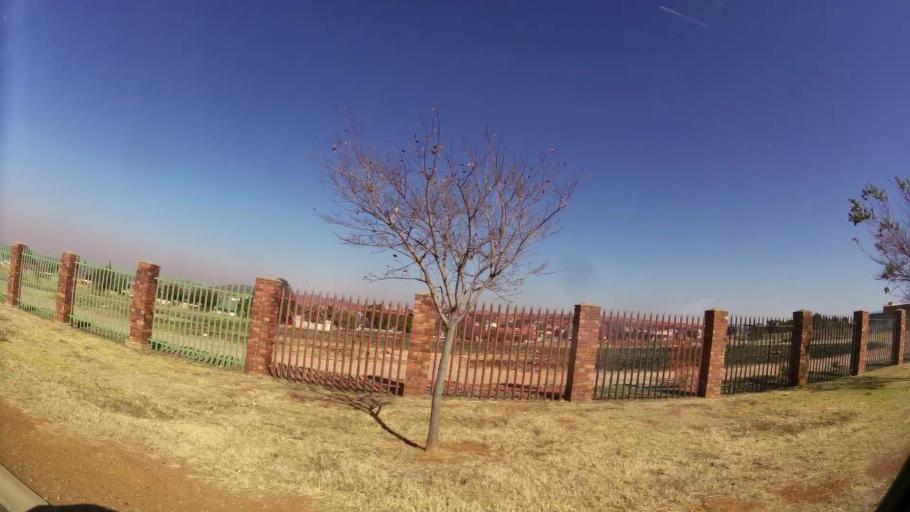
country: ZA
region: Gauteng
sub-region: Ekurhuleni Metropolitan Municipality
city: Germiston
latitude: -26.2500
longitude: 28.1138
